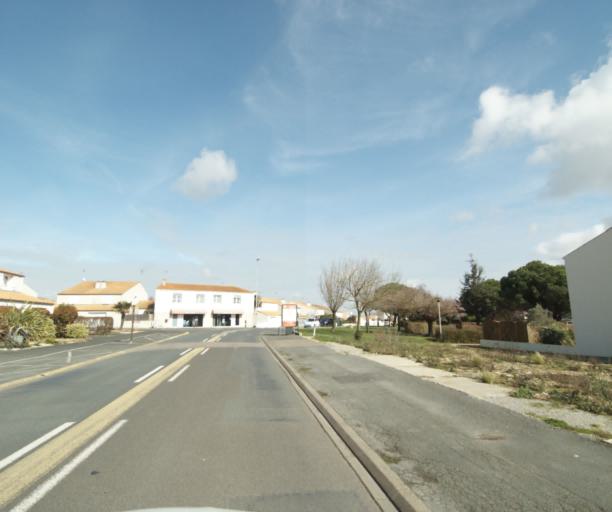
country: FR
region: Poitou-Charentes
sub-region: Departement de la Charente-Maritime
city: Lagord
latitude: 46.1831
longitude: -1.1613
